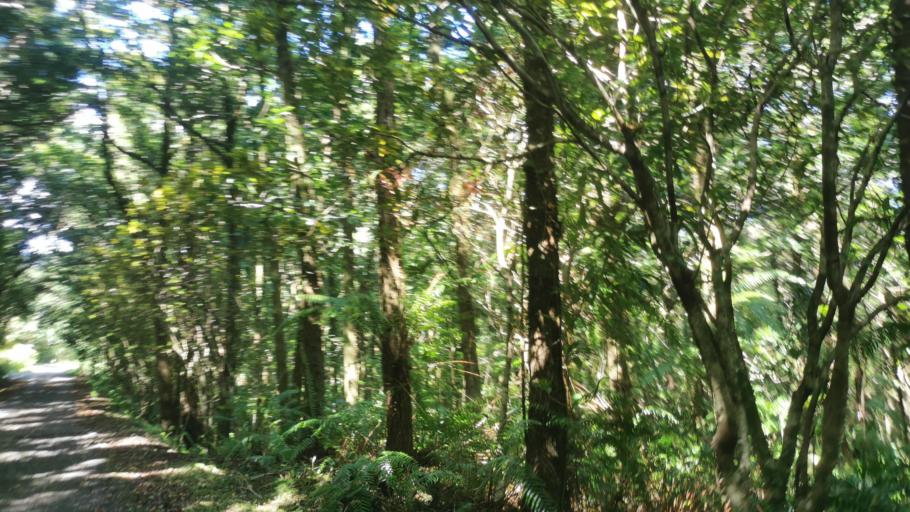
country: RE
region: Reunion
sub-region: Reunion
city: Saint-Philippe
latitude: -21.3560
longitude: 55.7391
